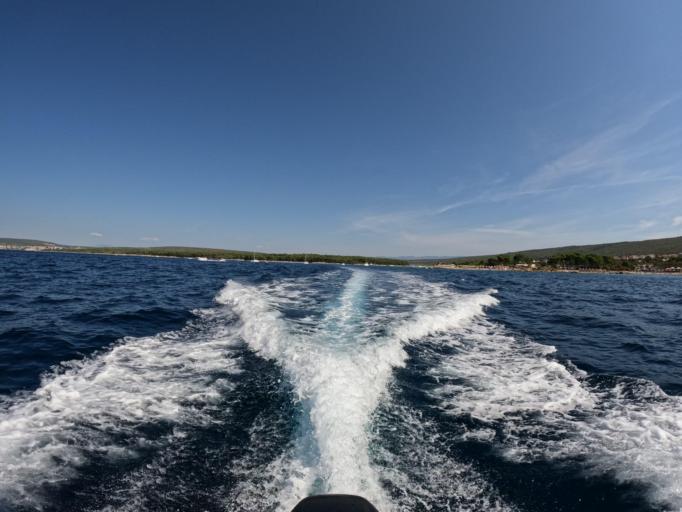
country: HR
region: Primorsko-Goranska
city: Punat
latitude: 45.0061
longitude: 14.6206
